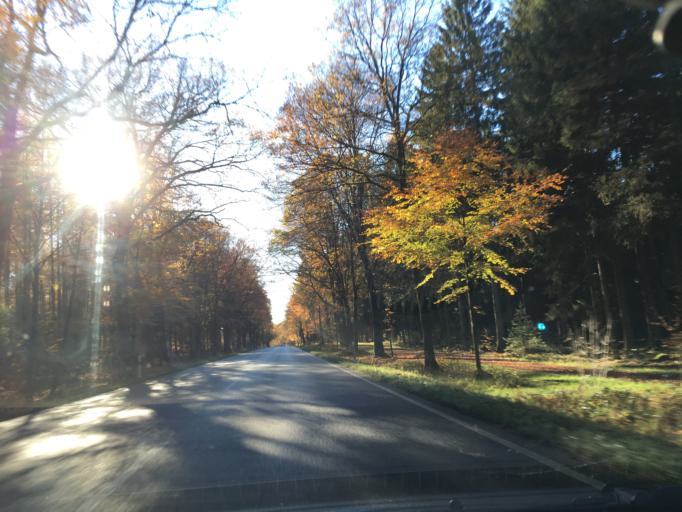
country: DE
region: Lower Saxony
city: Bispingen
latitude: 53.0359
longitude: 9.9824
